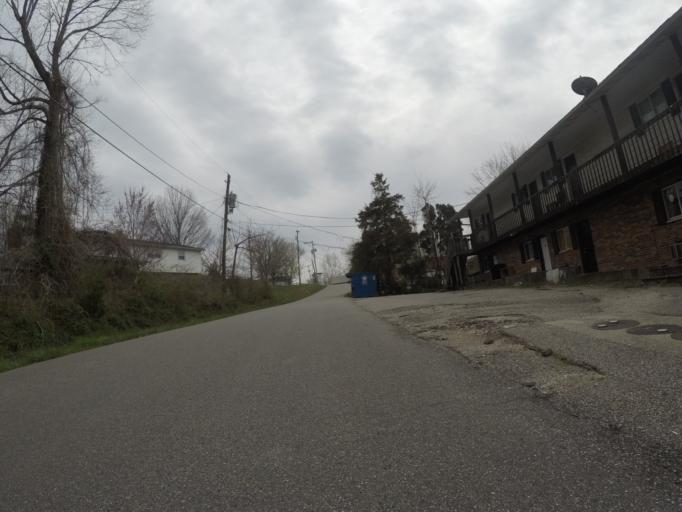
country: US
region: West Virginia
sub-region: Cabell County
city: Pea Ridge
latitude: 38.4183
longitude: -82.3224
